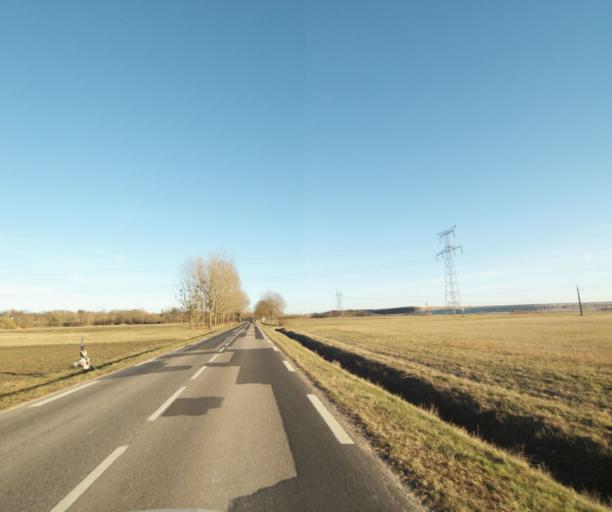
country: FR
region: Lorraine
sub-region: Departement de Meurthe-et-Moselle
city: Art-sur-Meurthe
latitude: 48.6598
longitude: 6.2508
